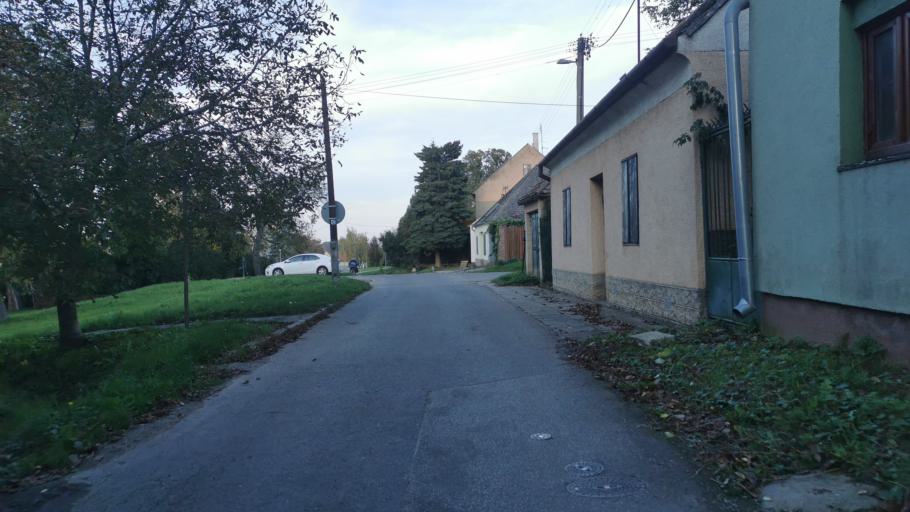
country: SK
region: Trnavsky
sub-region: Okres Skalica
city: Skalica
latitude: 48.8356
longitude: 17.2349
